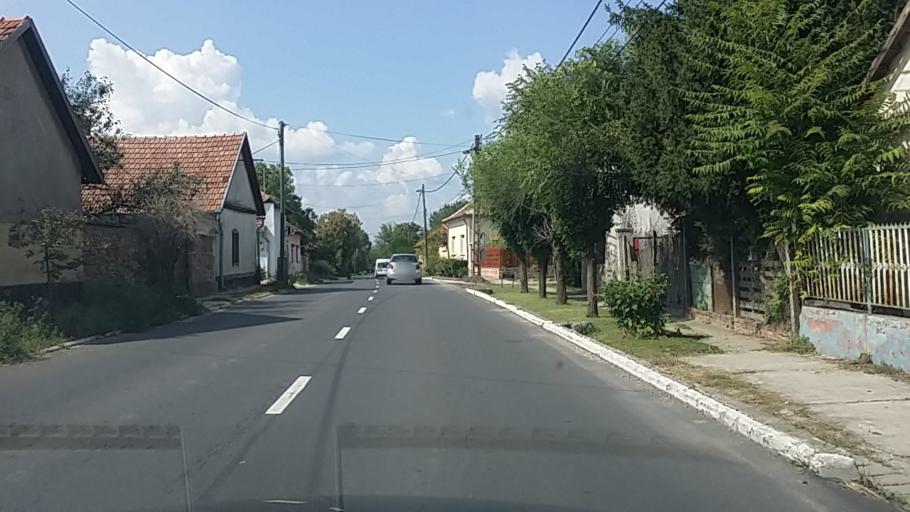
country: HU
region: Bacs-Kiskun
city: Tiszaalpar
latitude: 46.8253
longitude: 19.9820
